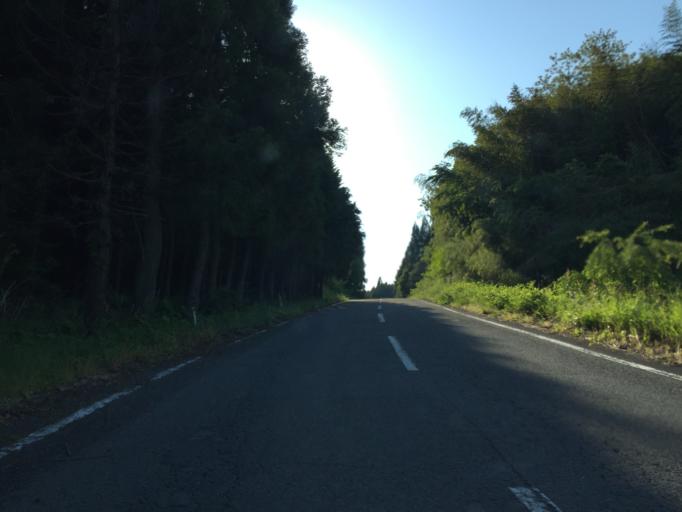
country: JP
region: Ibaraki
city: Daigo
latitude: 36.9266
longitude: 140.4661
